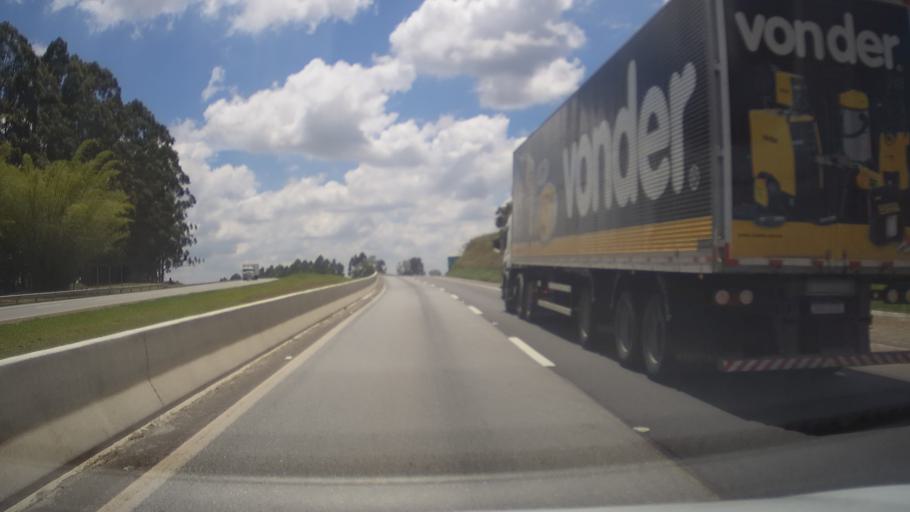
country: BR
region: Minas Gerais
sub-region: Campanha
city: Campanha
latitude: -21.7927
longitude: -45.4501
